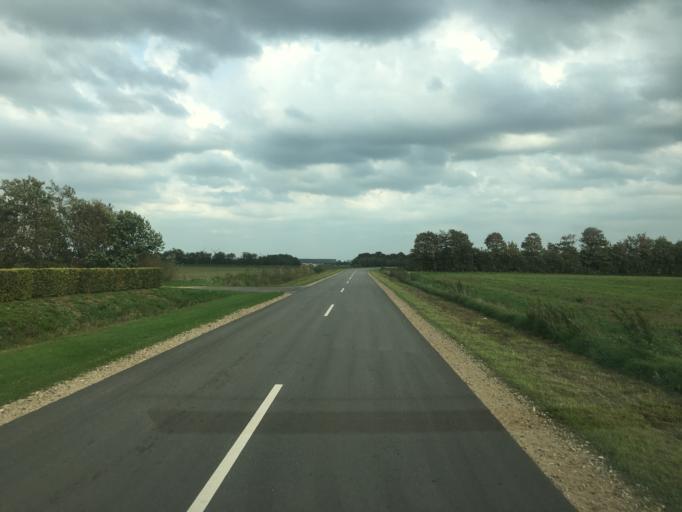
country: DK
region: South Denmark
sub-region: Tonder Kommune
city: Logumkloster
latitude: 55.0611
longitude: 8.9731
